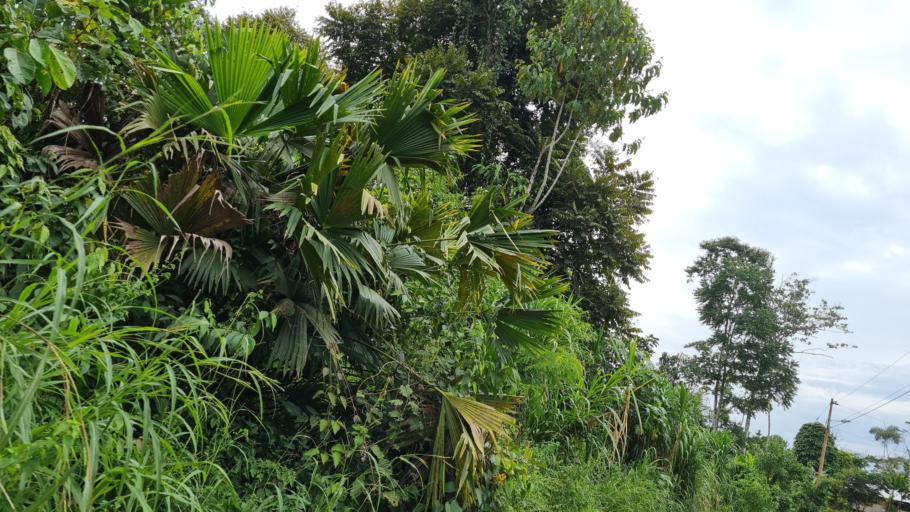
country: EC
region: Napo
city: Tena
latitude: -1.0003
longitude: -77.7607
